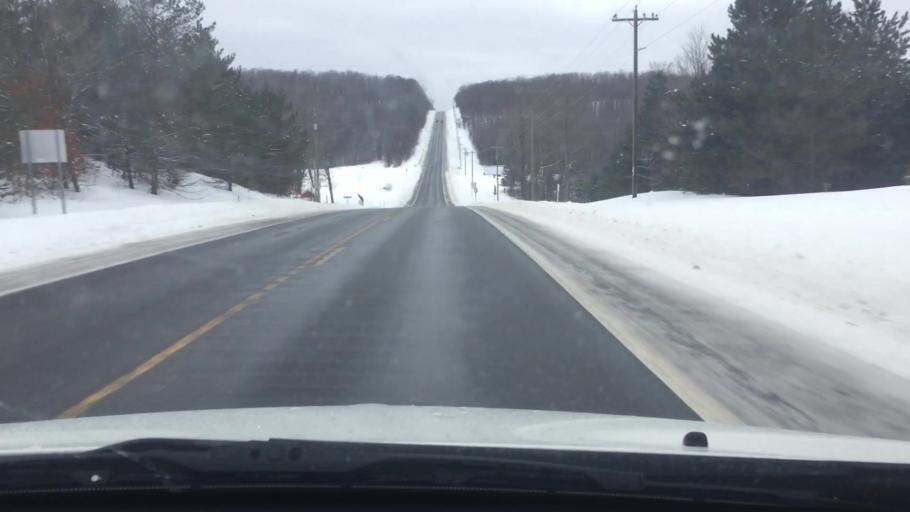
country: US
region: Michigan
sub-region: Charlevoix County
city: Boyne City
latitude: 45.0964
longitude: -84.9980
